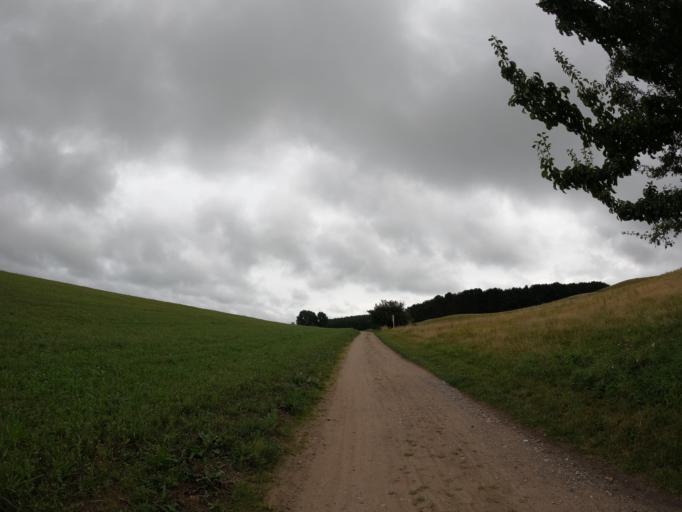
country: DE
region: Mecklenburg-Vorpommern
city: Ostseebad Gohren
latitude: 54.3065
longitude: 13.6912
